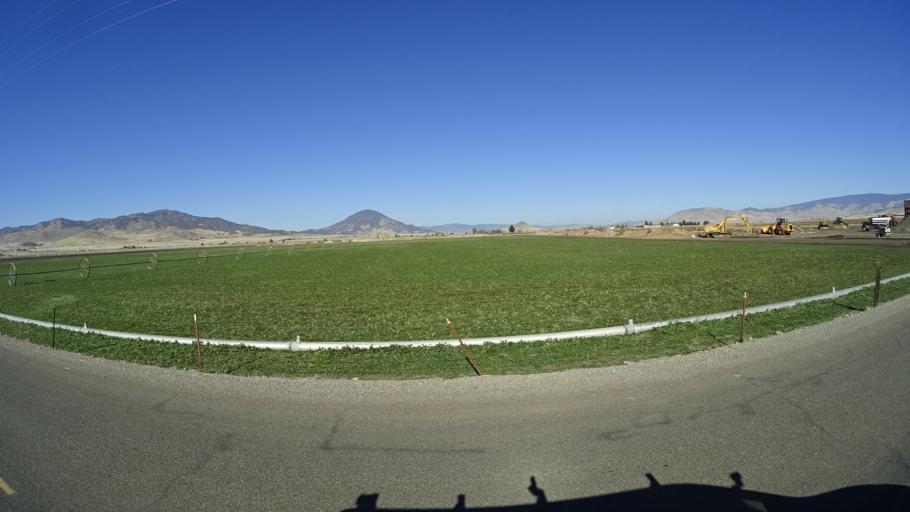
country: US
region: California
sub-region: Siskiyou County
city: Montague
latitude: 41.7561
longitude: -122.4877
